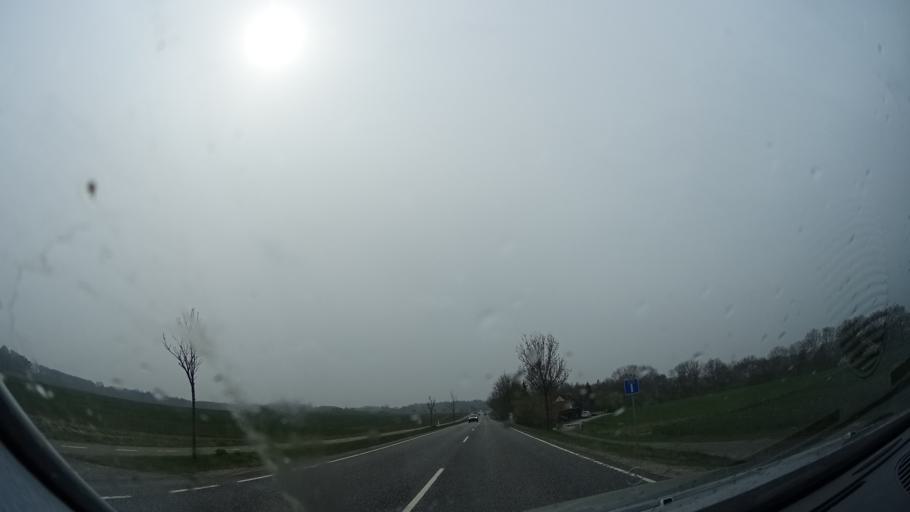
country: DK
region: Zealand
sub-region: Lejre Kommune
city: Ejby
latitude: 55.6755
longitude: 11.8343
